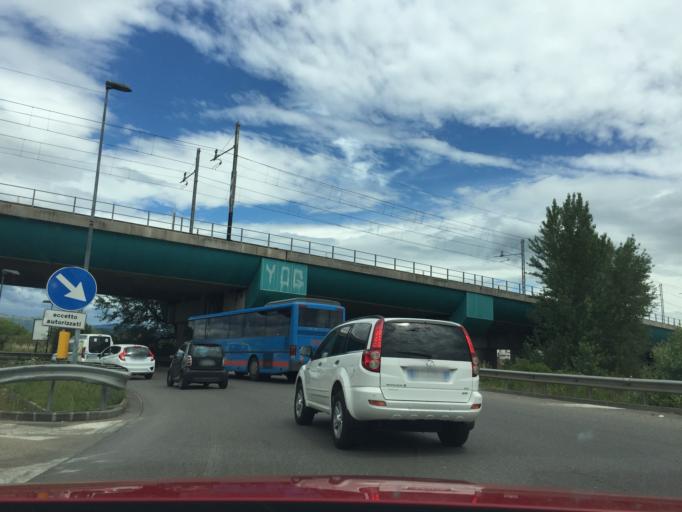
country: IT
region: Tuscany
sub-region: Province of Florence
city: Sesto Fiorentino
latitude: 43.8009
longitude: 11.2115
